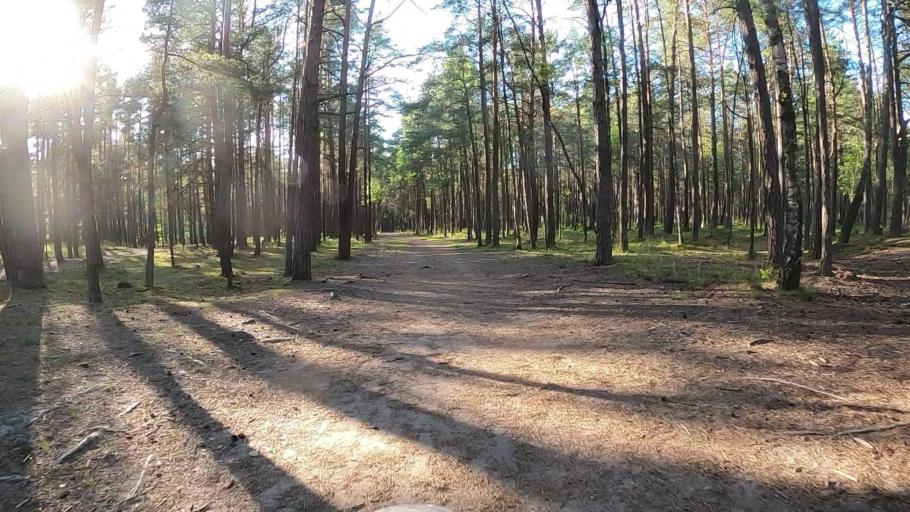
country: LV
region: Carnikava
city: Carnikava
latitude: 57.1368
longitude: 24.2463
